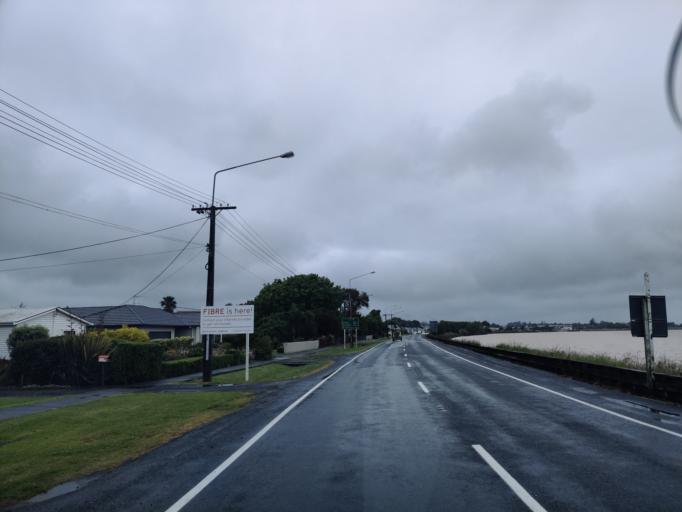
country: NZ
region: Northland
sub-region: Kaipara District
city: Dargaville
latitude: -35.9505
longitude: 173.8648
